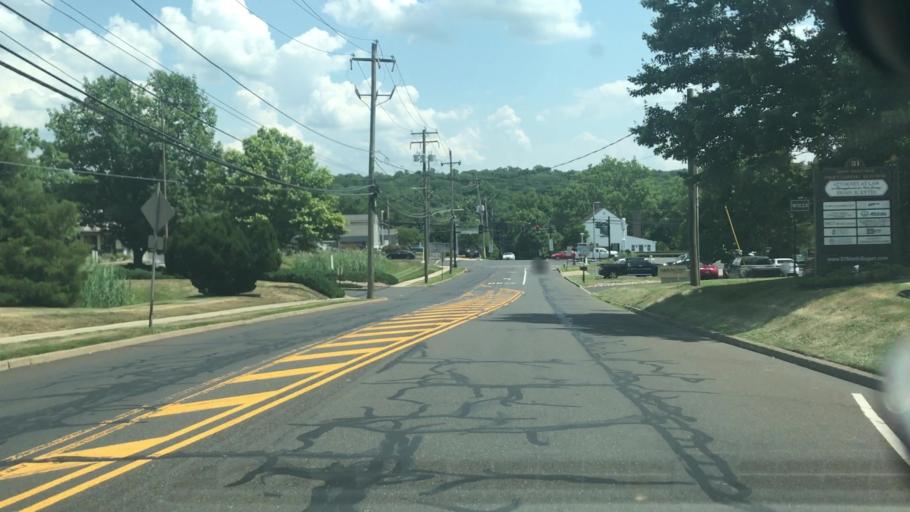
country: US
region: Pennsylvania
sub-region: Bucks County
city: New Hope
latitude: 40.3639
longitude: -74.9674
